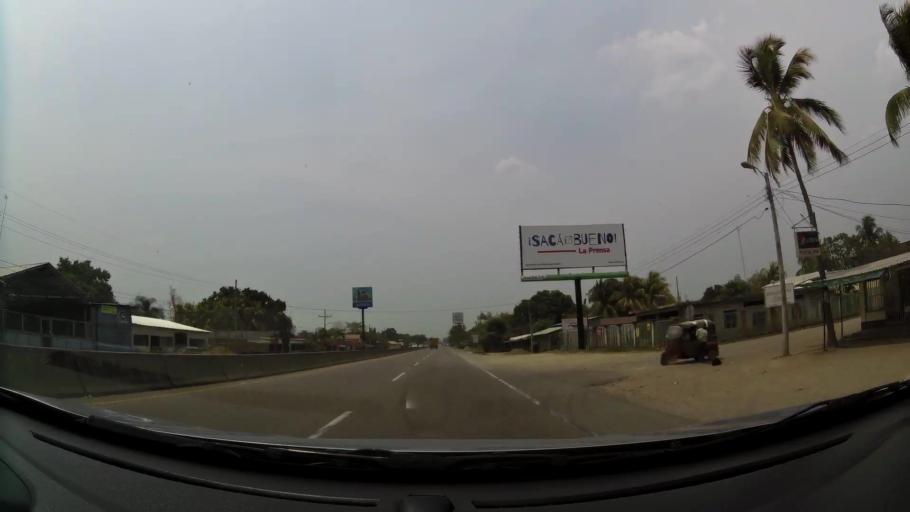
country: HN
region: Cortes
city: Oropendolas
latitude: 15.0426
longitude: -87.9282
